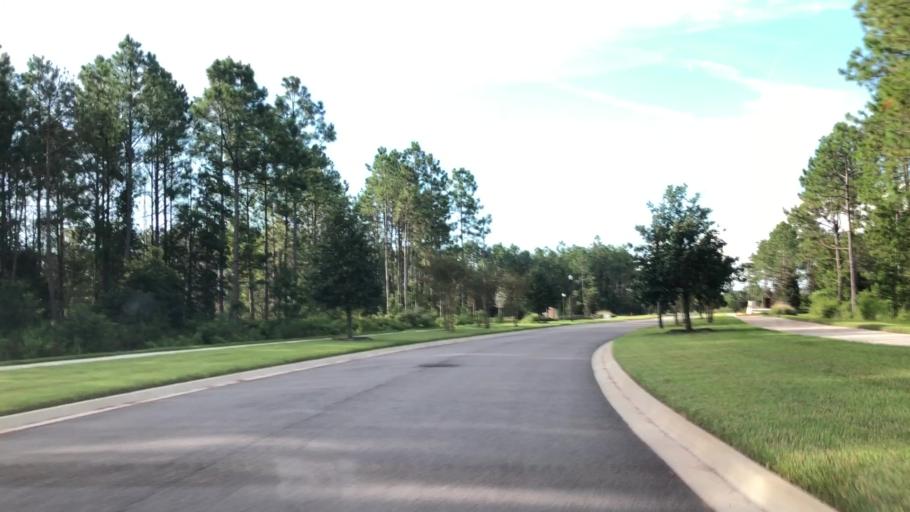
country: US
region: Florida
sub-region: Saint Johns County
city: Palm Valley
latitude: 30.1333
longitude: -81.4024
